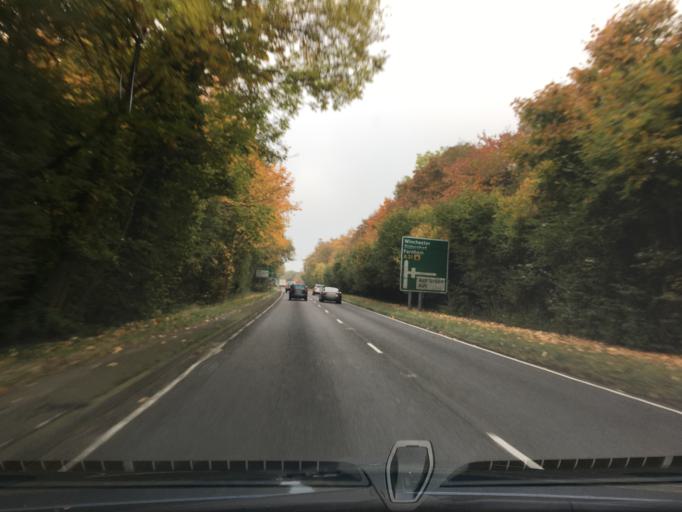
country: GB
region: England
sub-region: Surrey
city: Seale
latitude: 51.2268
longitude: -0.7072
